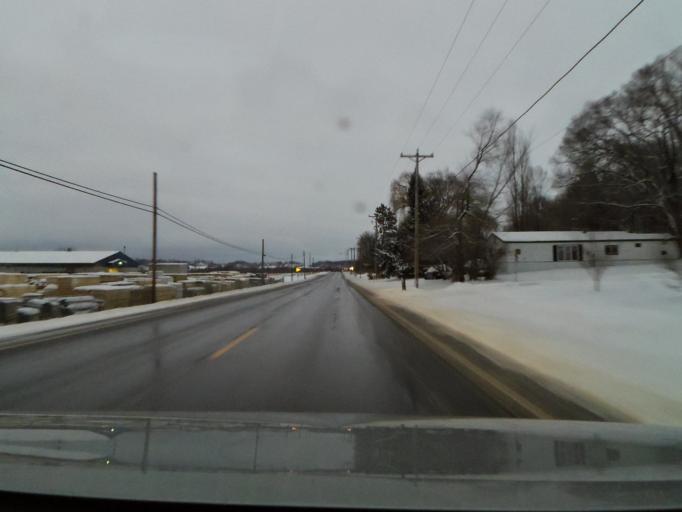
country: US
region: Wisconsin
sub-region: Dunn County
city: Boyceville
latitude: 44.9554
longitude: -92.0682
